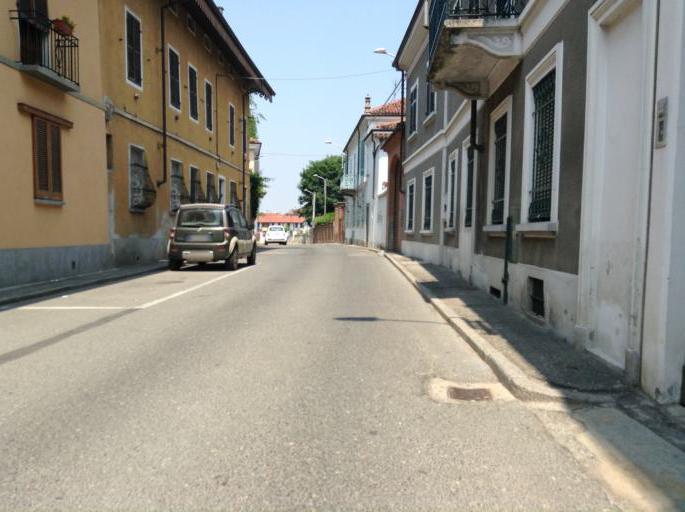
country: IT
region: Piedmont
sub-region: Provincia di Torino
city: Carignano
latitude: 44.9093
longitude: 7.6732
